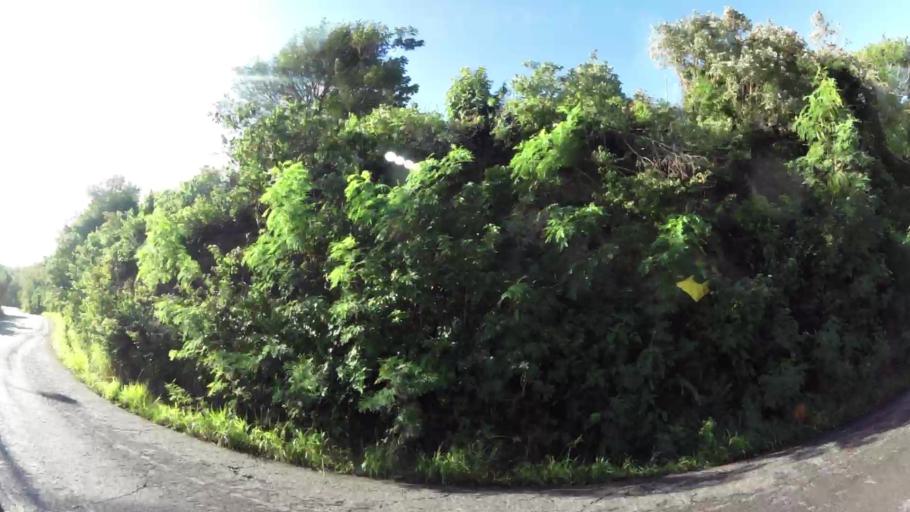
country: LC
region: Anse-la-Raye
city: Anse La Raye
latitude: 13.9248
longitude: -61.0442
